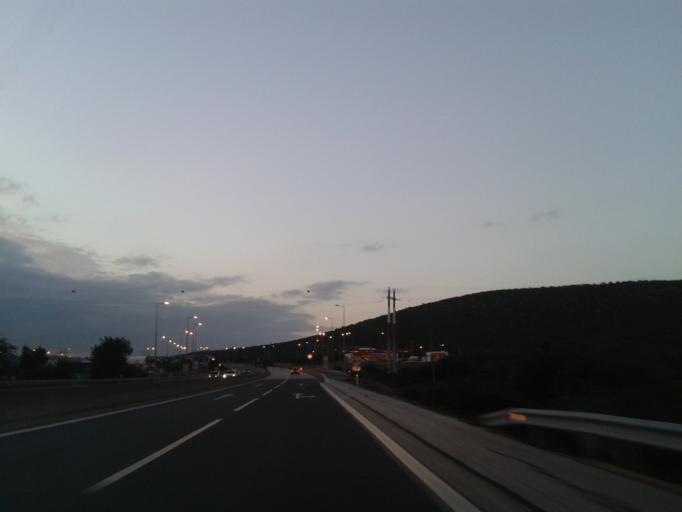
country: PT
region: Faro
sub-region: Loule
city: Boliqueime
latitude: 37.1346
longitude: -8.1079
